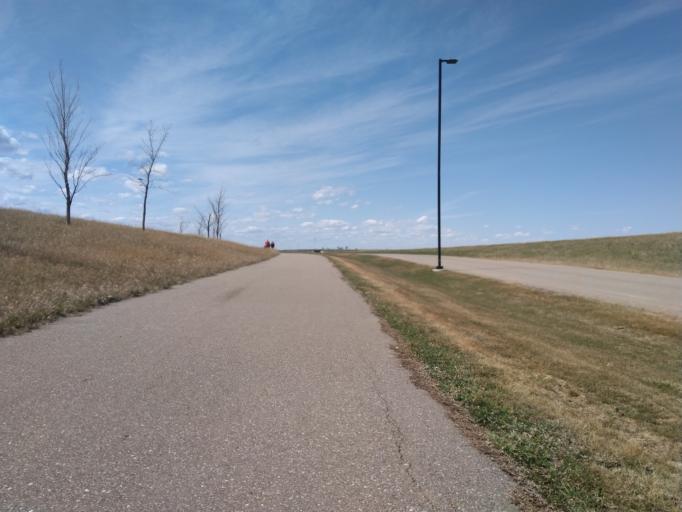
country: CA
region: Alberta
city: Chestermere
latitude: 50.9385
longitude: -113.9054
